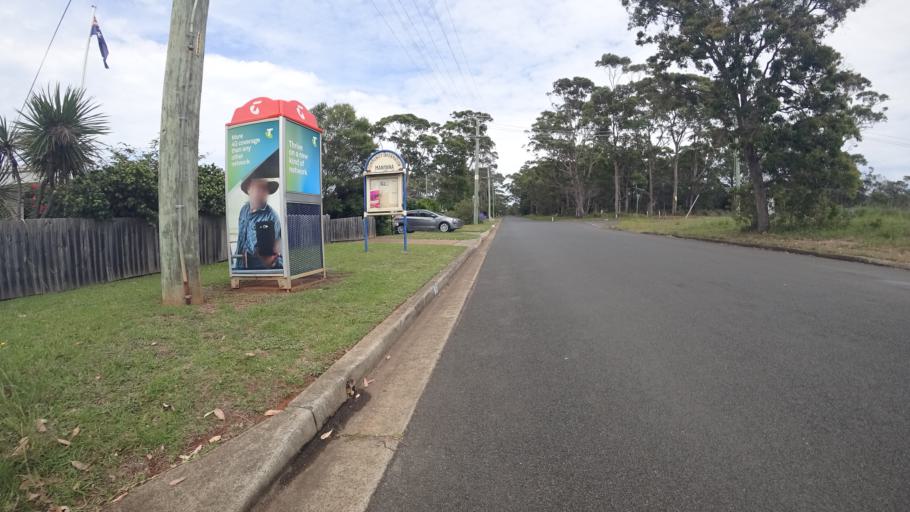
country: AU
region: New South Wales
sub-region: Shoalhaven Shire
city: Milton
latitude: -35.2552
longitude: 150.5153
